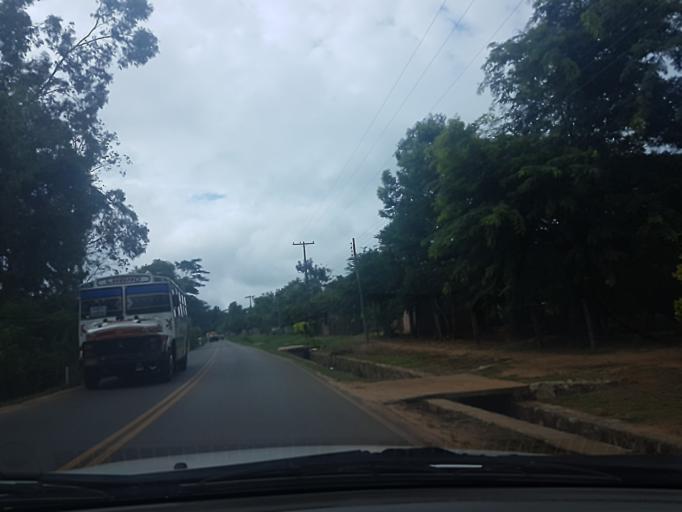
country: PY
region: Central
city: Limpio
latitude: -25.2109
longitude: -57.4492
